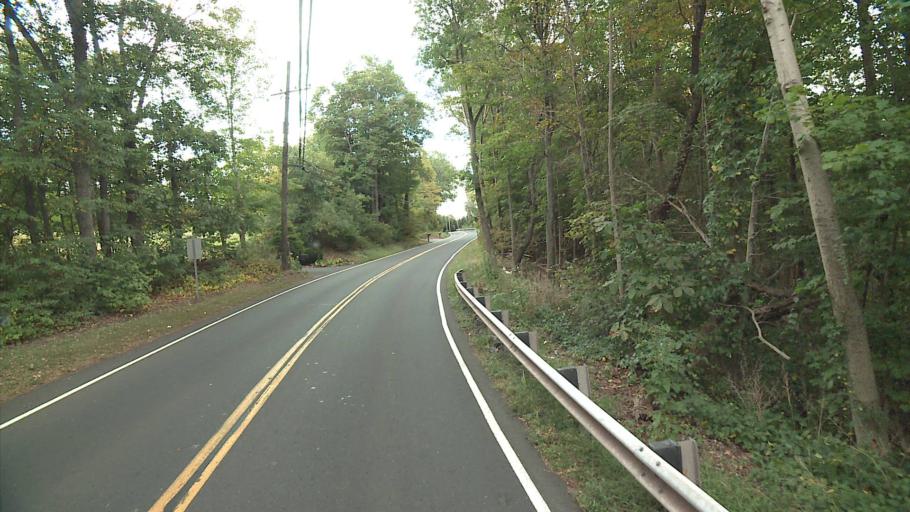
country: US
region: Connecticut
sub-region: Middlesex County
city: Durham
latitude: 41.4808
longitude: -72.7253
